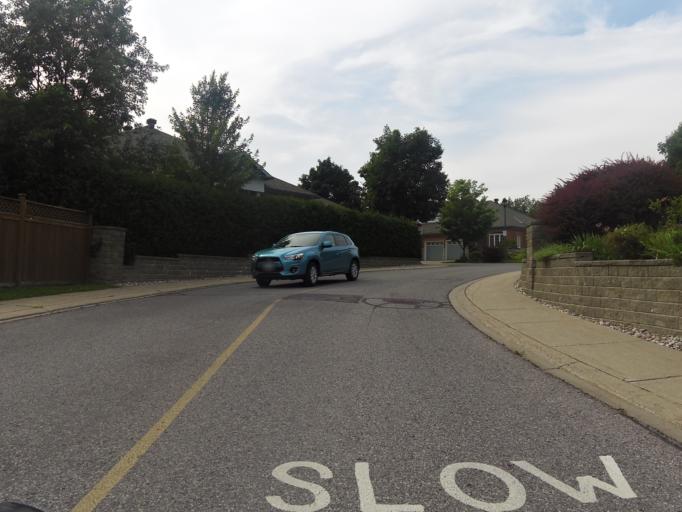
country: CA
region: Ontario
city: Bells Corners
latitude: 45.3145
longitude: -75.9235
